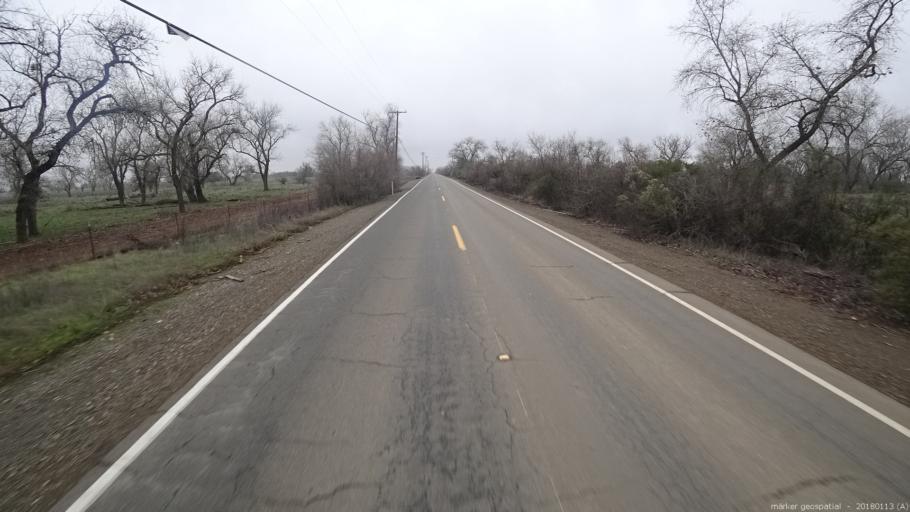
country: US
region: California
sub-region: Sacramento County
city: Gold River
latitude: 38.5931
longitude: -121.2076
